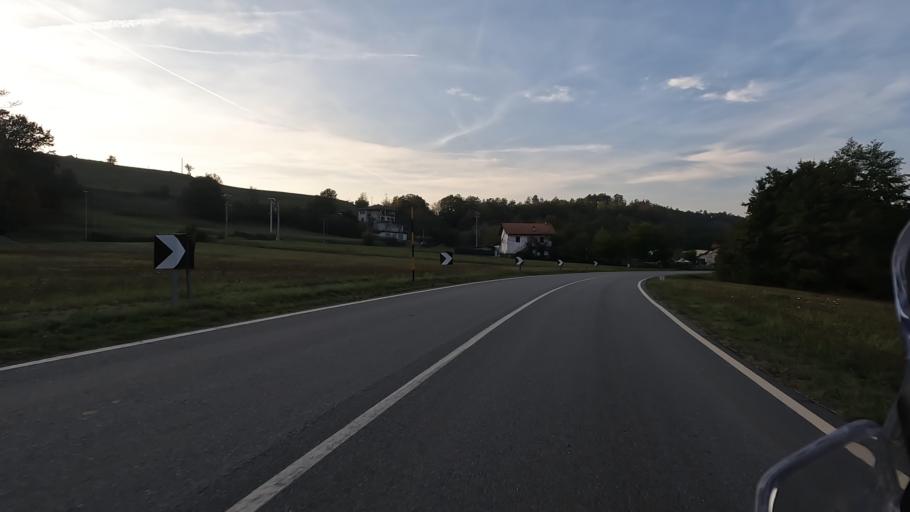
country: IT
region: Liguria
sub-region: Provincia di Savona
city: Sassello
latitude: 44.5109
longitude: 8.4746
